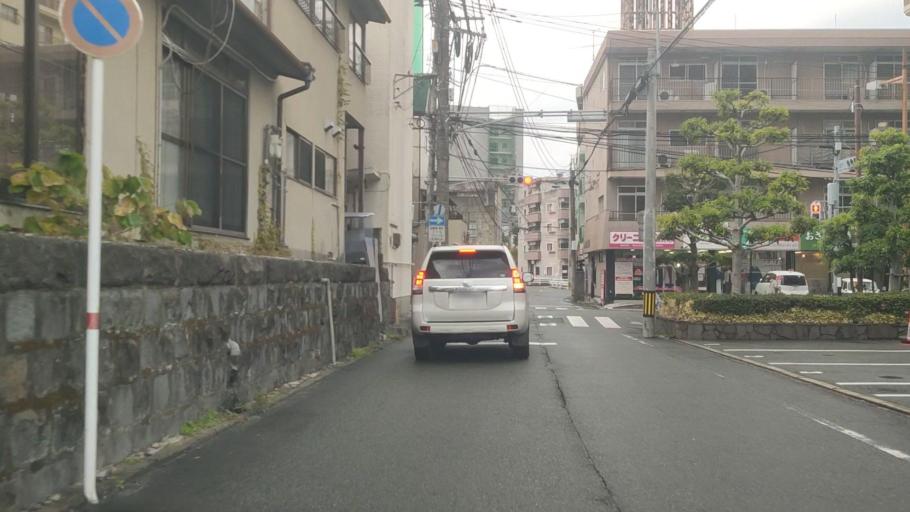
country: JP
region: Kumamoto
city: Kumamoto
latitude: 32.7919
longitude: 130.7304
